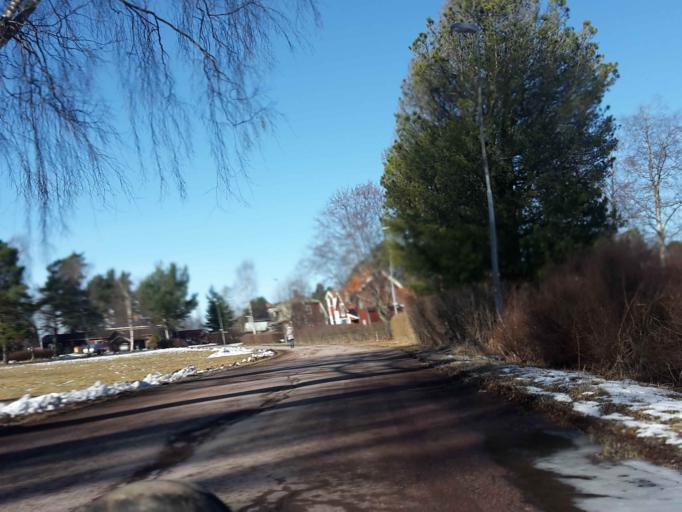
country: SE
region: Dalarna
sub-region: Orsa Kommun
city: Orsa
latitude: 61.1187
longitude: 14.6076
